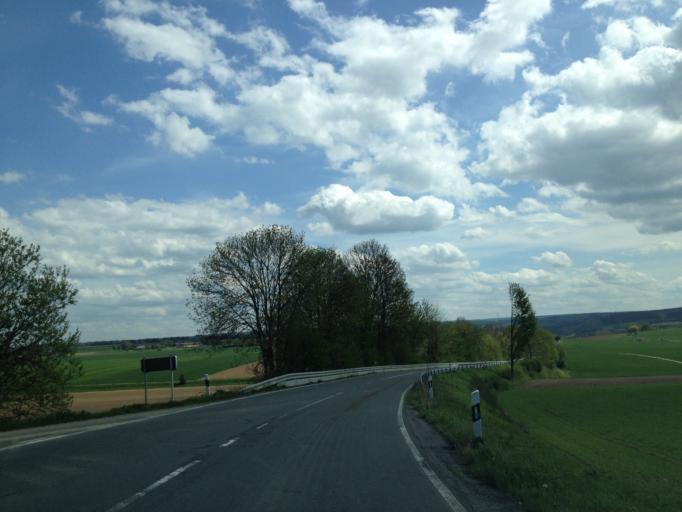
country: DE
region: North Rhine-Westphalia
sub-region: Regierungsbezirk Arnsberg
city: Mohnesee
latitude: 51.5015
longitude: 8.2082
